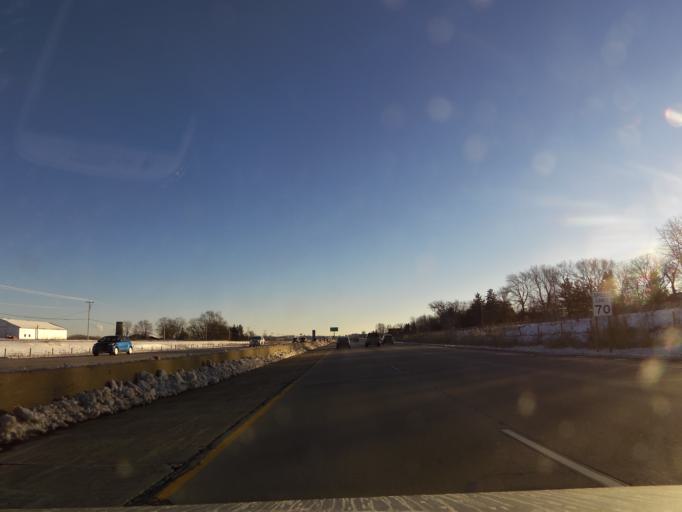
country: US
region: Wisconsin
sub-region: Kenosha County
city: Somers
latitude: 42.6317
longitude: -87.9527
